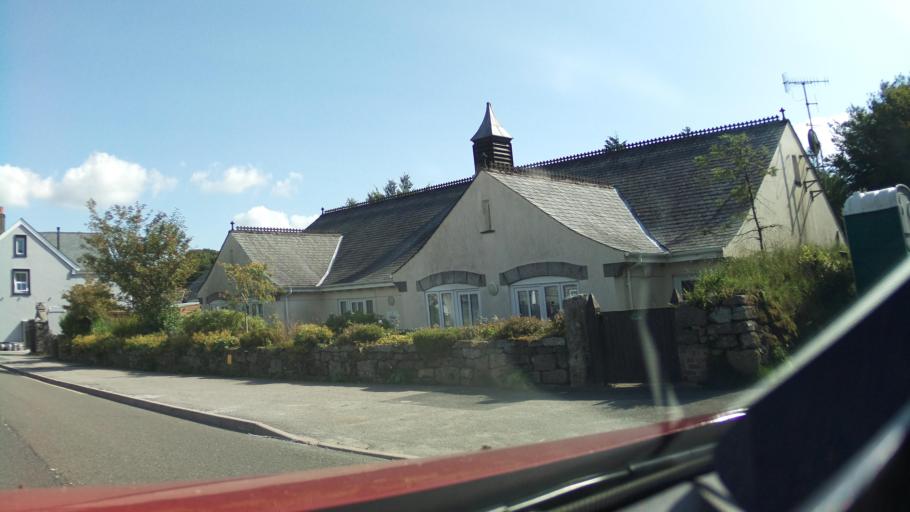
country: GB
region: England
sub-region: Devon
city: Yelverton
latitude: 50.5453
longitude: -3.9934
